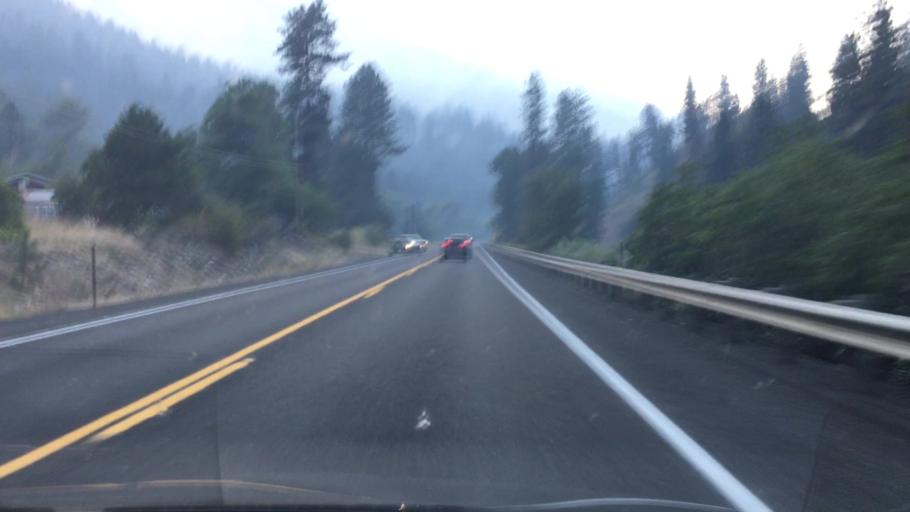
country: US
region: Idaho
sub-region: Valley County
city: McCall
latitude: 45.2366
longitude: -116.3274
